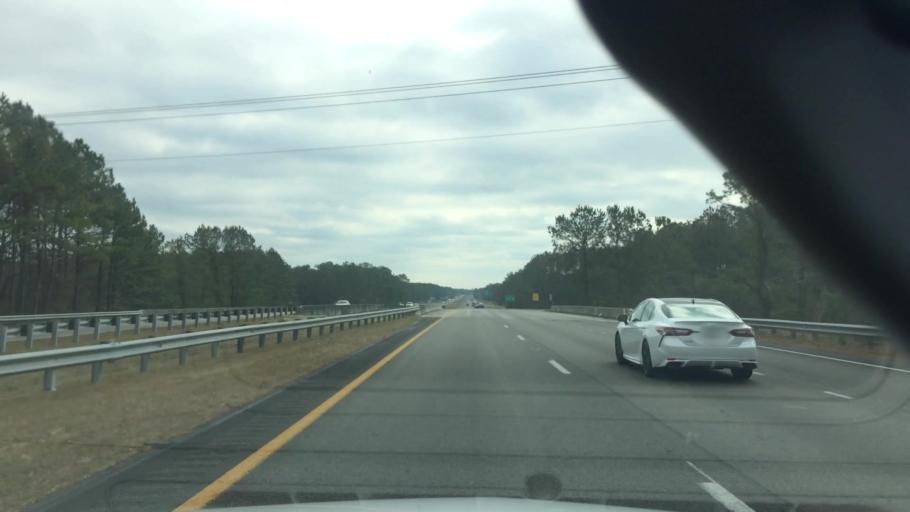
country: US
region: North Carolina
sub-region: New Hanover County
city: Castle Hayne
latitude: 34.3539
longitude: -77.8854
